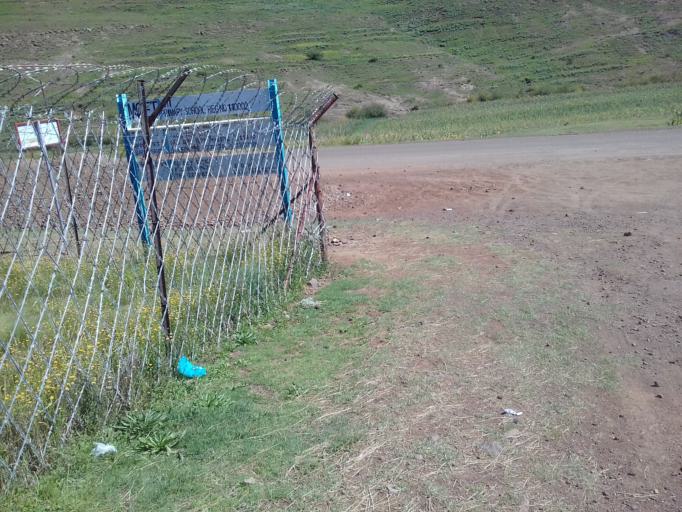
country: LS
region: Thaba-Tseka
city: Thaba-Tseka
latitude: -29.5198
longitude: 28.5820
